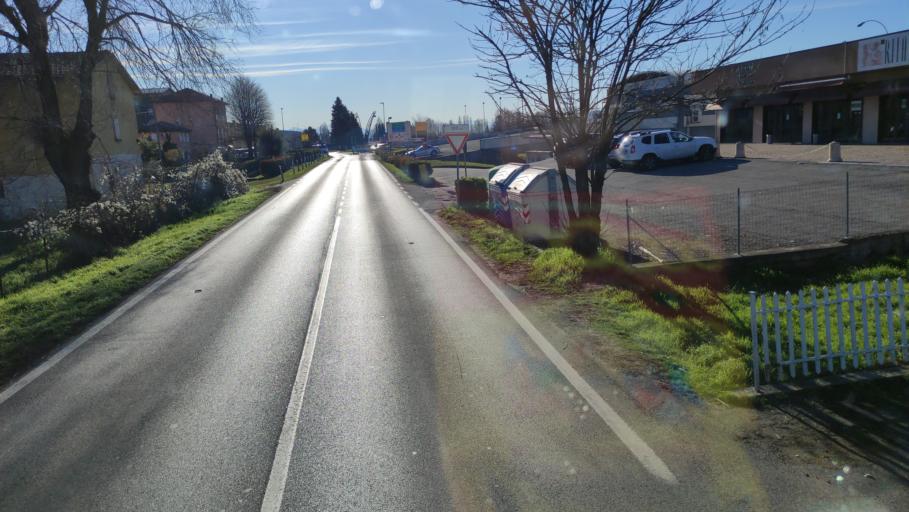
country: IT
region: Emilia-Romagna
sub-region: Provincia di Reggio Emilia
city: Novellara
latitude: 44.8365
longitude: 10.7142
